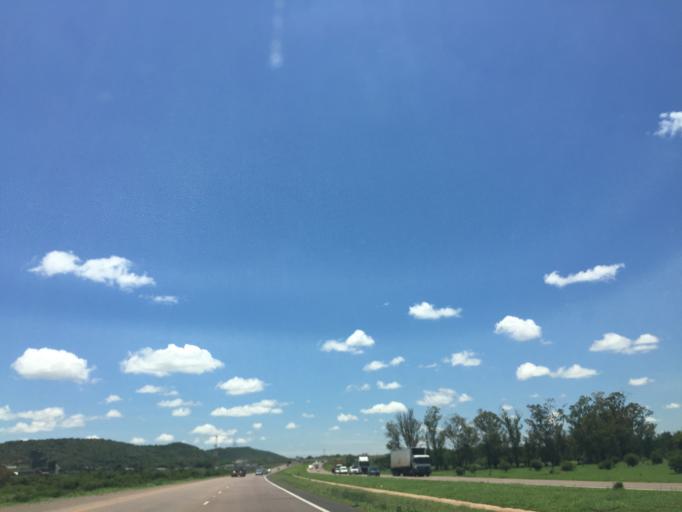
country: ZA
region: Gauteng
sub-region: City of Tshwane Metropolitan Municipality
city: Pretoria
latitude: -25.6386
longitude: 28.1902
